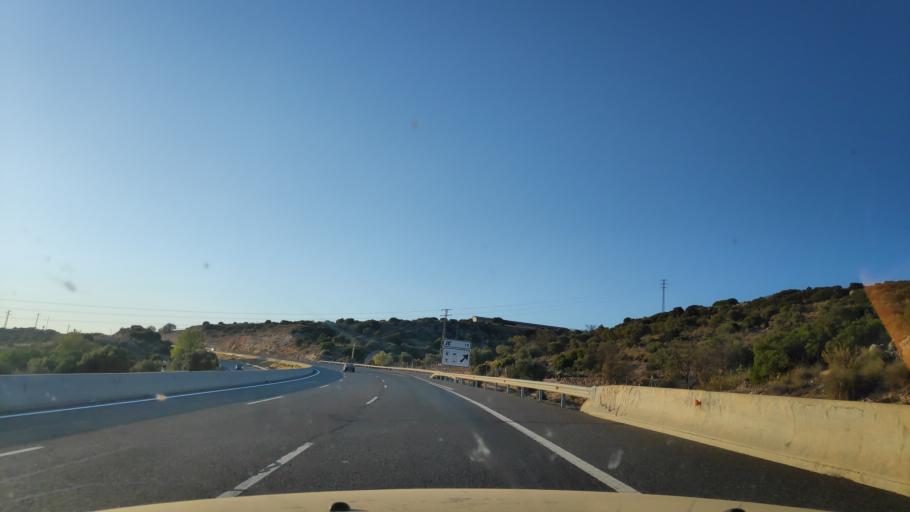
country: ES
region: Madrid
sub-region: Provincia de Madrid
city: Perales de Tajuna
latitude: 40.2446
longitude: -3.3457
